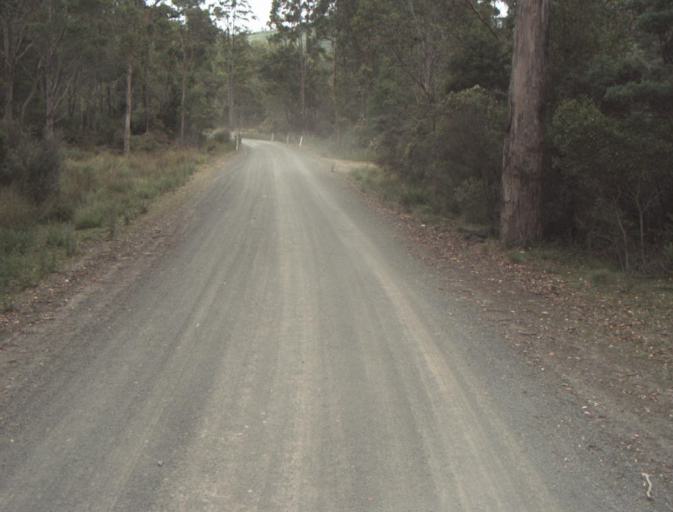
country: AU
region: Tasmania
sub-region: Dorset
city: Scottsdale
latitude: -41.4737
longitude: 147.6407
